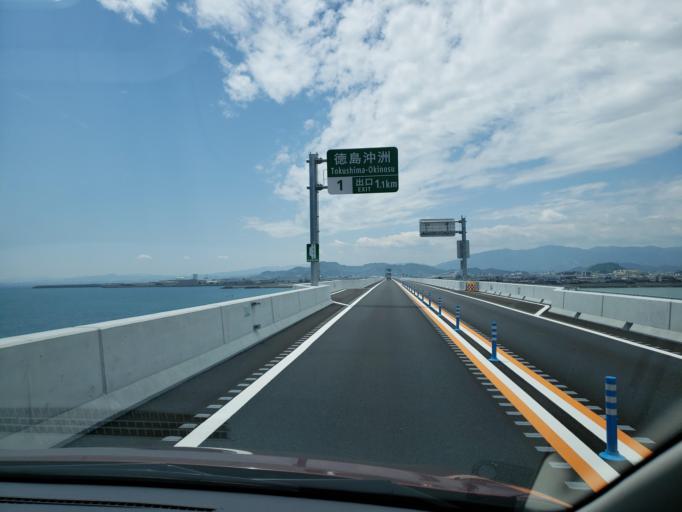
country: JP
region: Tokushima
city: Tokushima-shi
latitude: 34.0781
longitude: 134.6004
